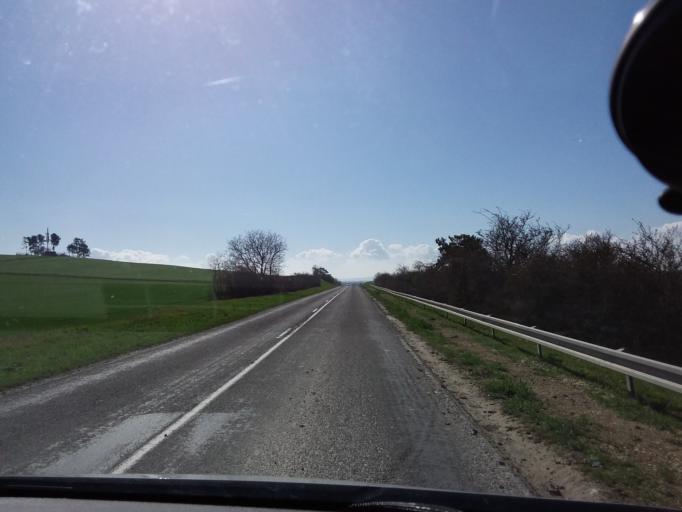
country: FR
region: Picardie
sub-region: Departement de l'Aisne
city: Guignicourt
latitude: 49.4522
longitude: 4.0396
